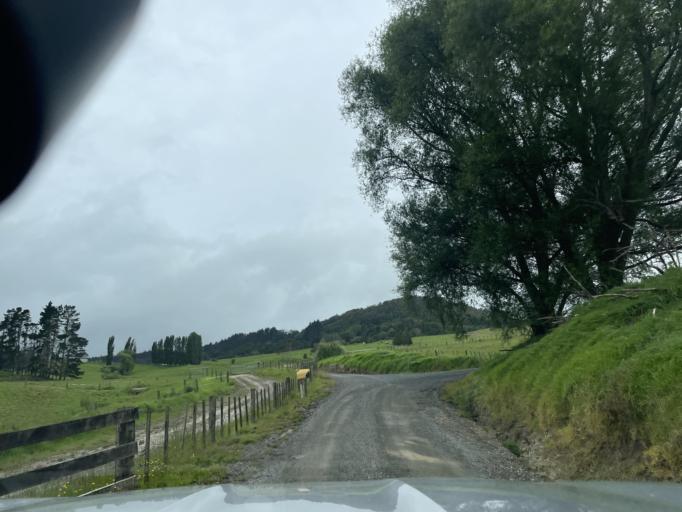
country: NZ
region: Northland
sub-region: Whangarei
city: Ruakaka
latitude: -36.0972
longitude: 174.4190
